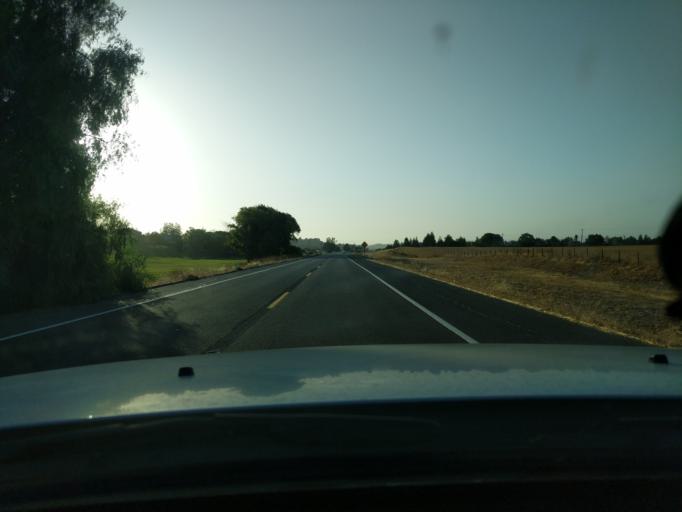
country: US
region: California
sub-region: San Benito County
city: Ridgemark
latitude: 36.8155
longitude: -121.3588
